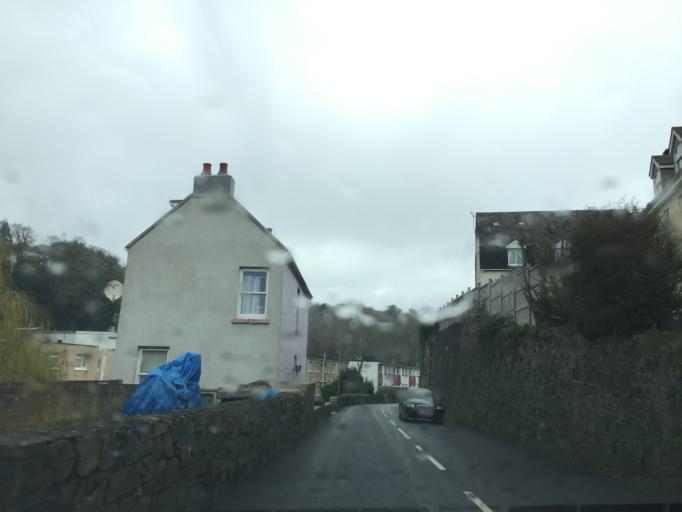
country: JE
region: St Helier
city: Saint Helier
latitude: 49.2029
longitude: -2.1551
